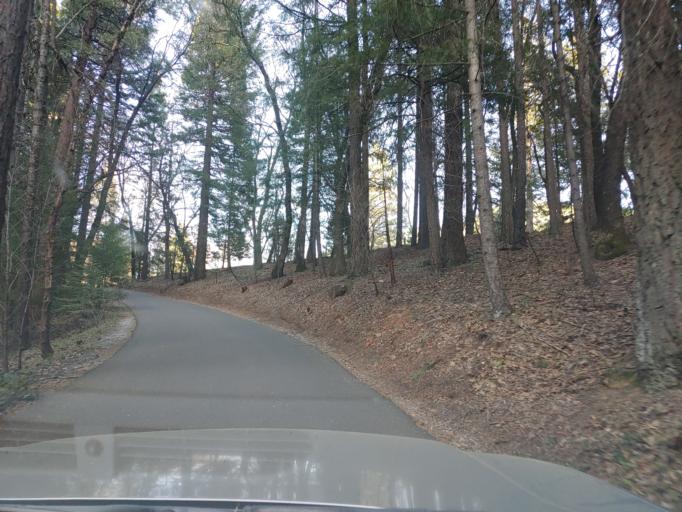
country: US
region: California
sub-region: Siskiyou County
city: Dunsmuir
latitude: 41.2252
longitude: -122.2784
